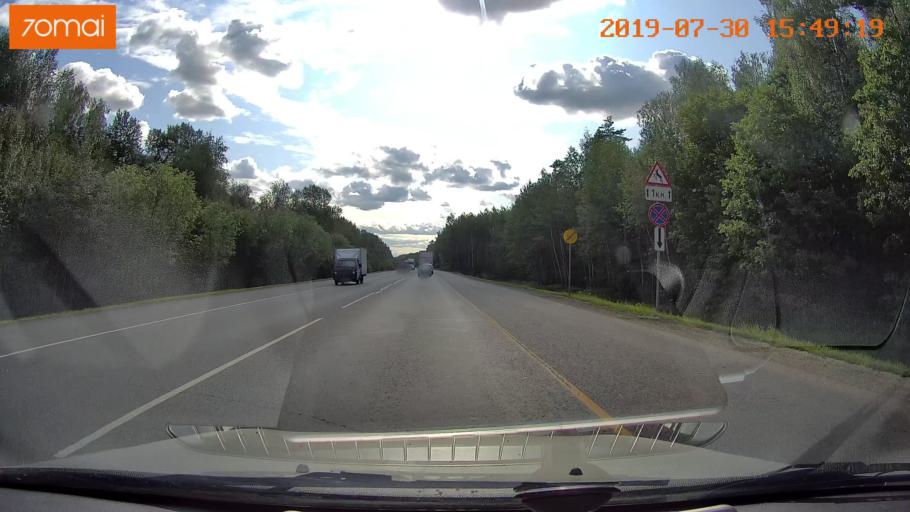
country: RU
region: Moskovskaya
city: Voskresensk
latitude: 55.3383
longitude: 38.6693
